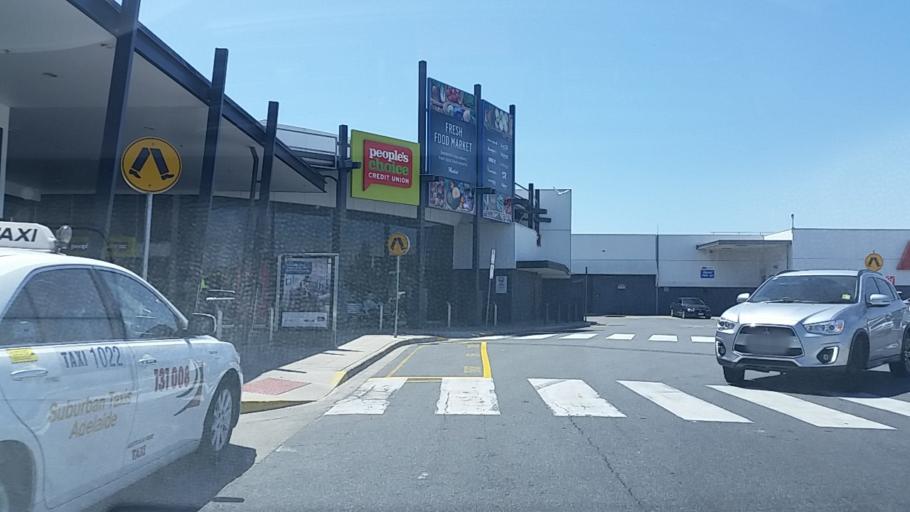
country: AU
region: South Australia
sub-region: Charles Sturt
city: Grange
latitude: -34.8810
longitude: 138.4922
